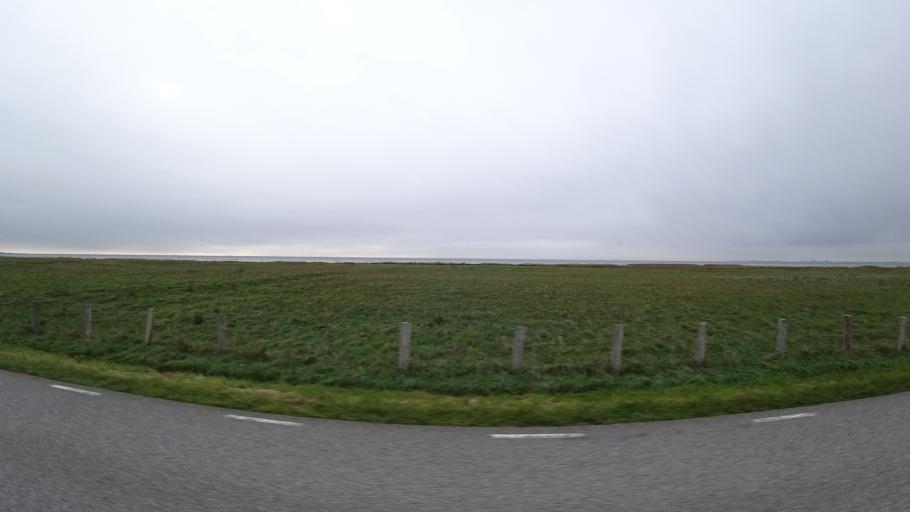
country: SE
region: Skane
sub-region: Kavlinge Kommun
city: Hofterup
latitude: 55.7955
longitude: 12.9379
